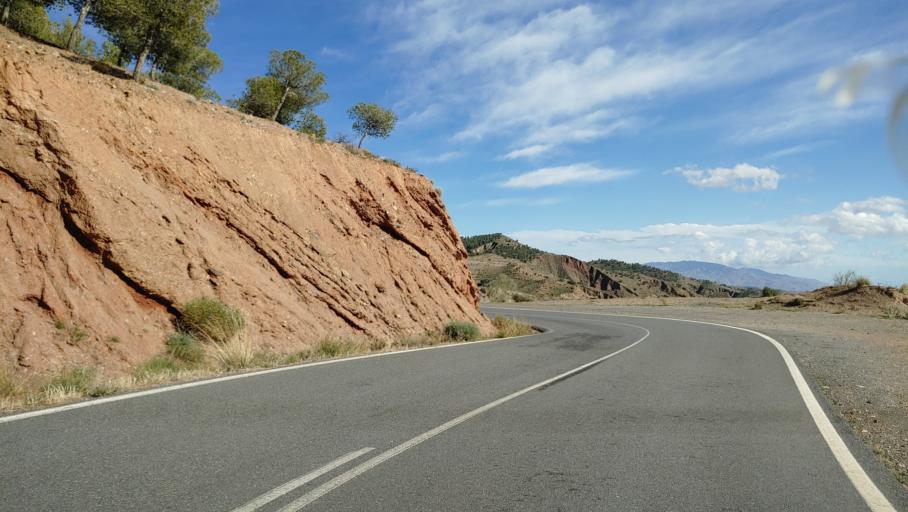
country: ES
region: Andalusia
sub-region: Provincia de Almeria
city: Canjayar
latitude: 37.0202
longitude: -2.7236
